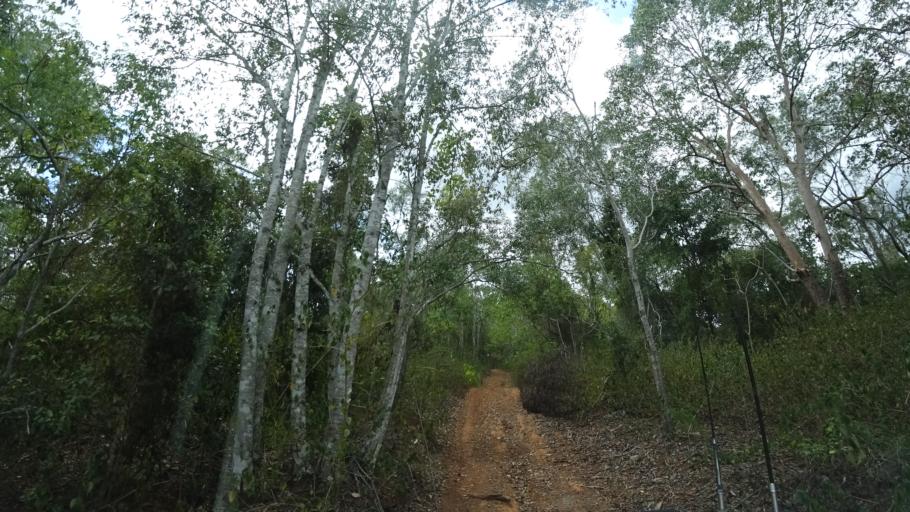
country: AU
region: Queensland
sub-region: Moreton Bay
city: Highvale
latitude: -27.4151
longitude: 152.7345
